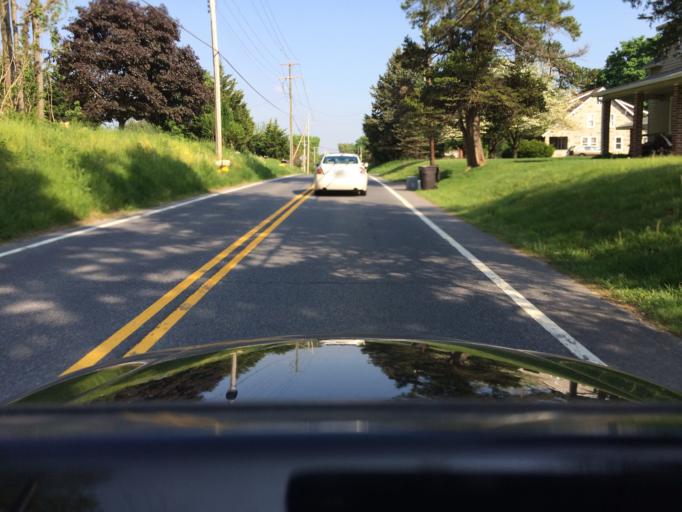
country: US
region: Maryland
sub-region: Carroll County
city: Eldersburg
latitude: 39.4281
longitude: -77.0059
